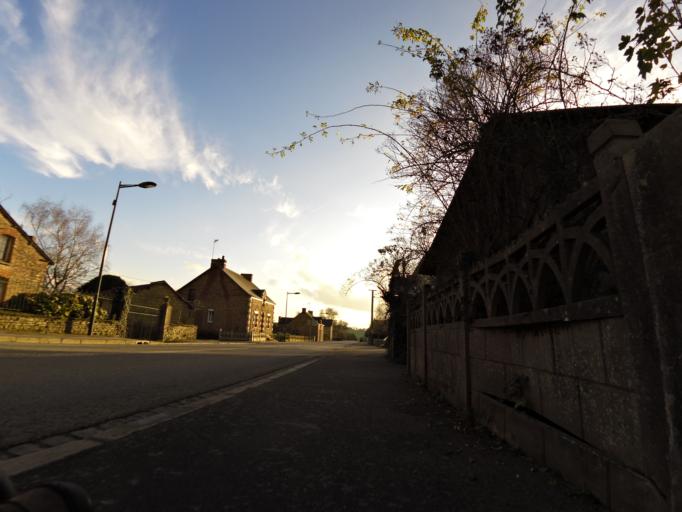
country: FR
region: Brittany
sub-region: Departement d'Ille-et-Vilaine
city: Pance
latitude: 47.8955
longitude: -1.6090
